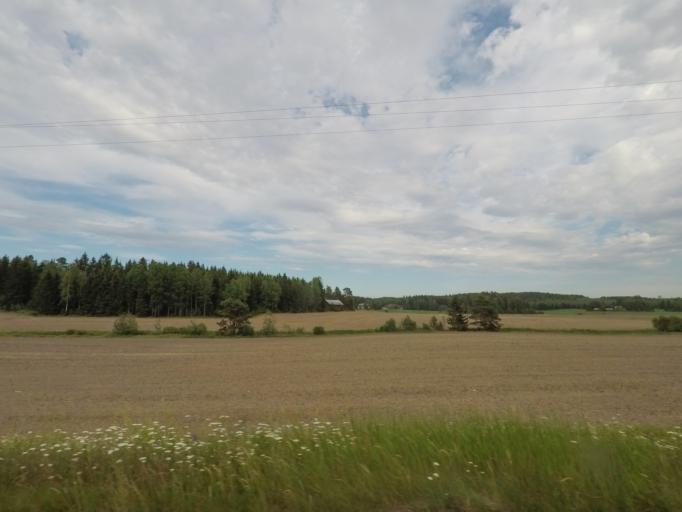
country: FI
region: Paijanne Tavastia
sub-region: Lahti
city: Hollola
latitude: 60.8603
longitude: 25.5005
